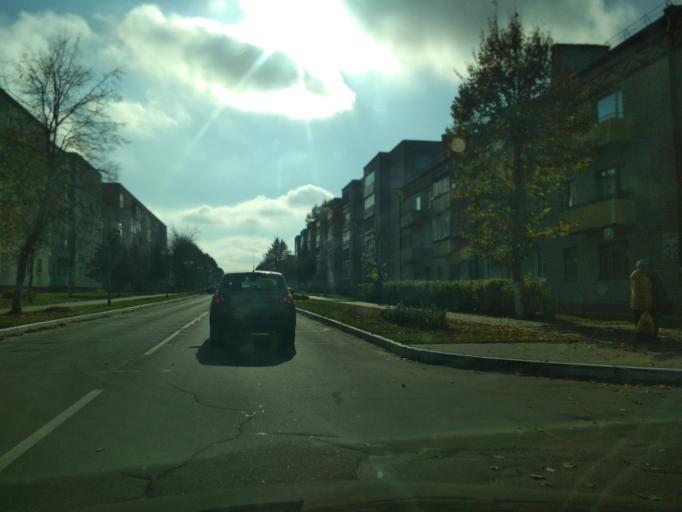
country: BY
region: Minsk
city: Mar''ina Horka
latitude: 53.5146
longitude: 28.1456
